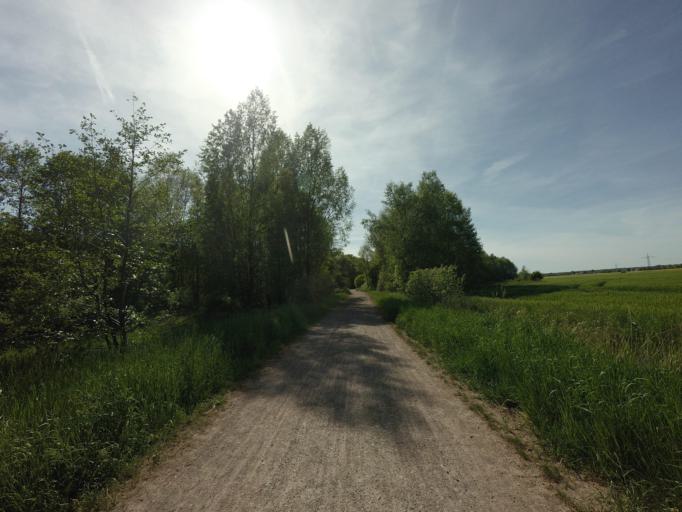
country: DE
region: Lower Saxony
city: Cremlingen
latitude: 52.2917
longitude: 10.6207
